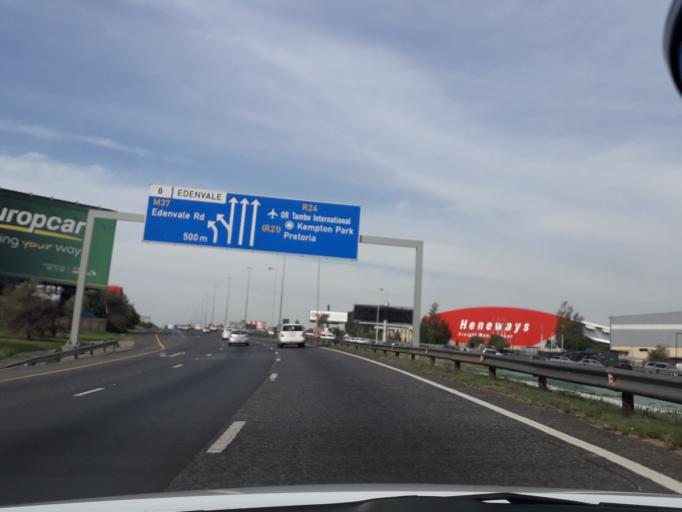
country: ZA
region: Gauteng
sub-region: City of Johannesburg Metropolitan Municipality
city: Modderfontein
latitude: -26.1628
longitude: 28.1563
